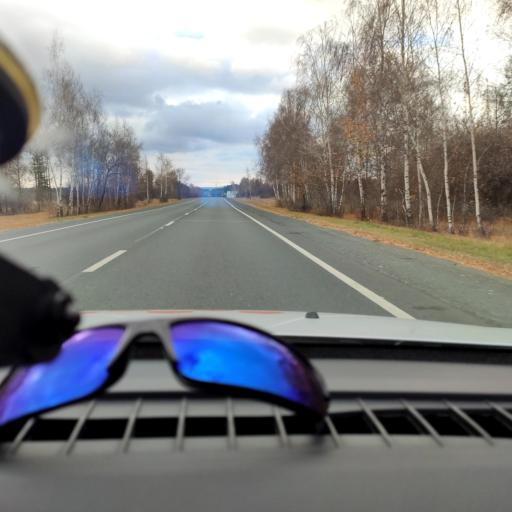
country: RU
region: Samara
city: Volzhskiy
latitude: 53.4612
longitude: 50.1273
